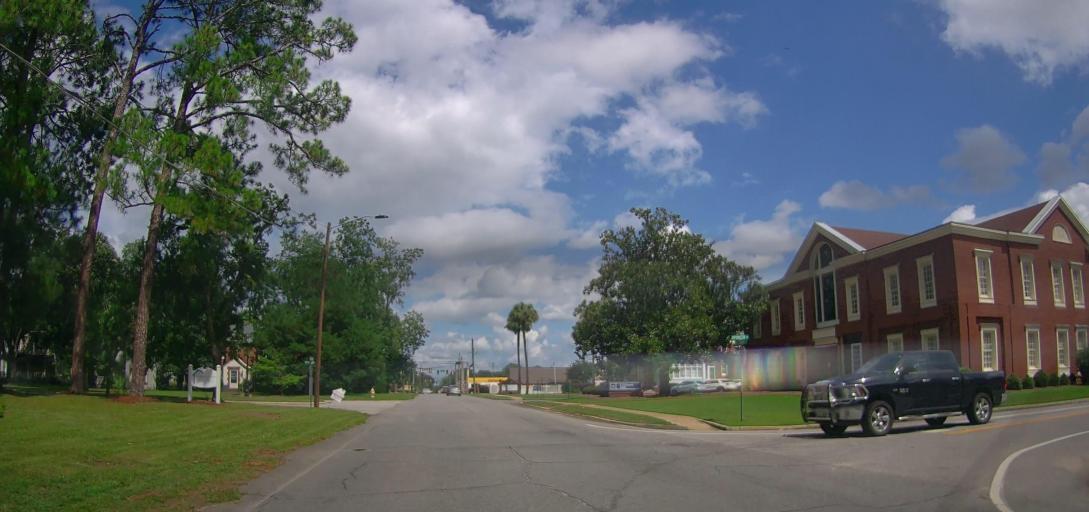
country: US
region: Georgia
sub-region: Ben Hill County
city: Fitzgerald
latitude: 31.7059
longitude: -83.2547
